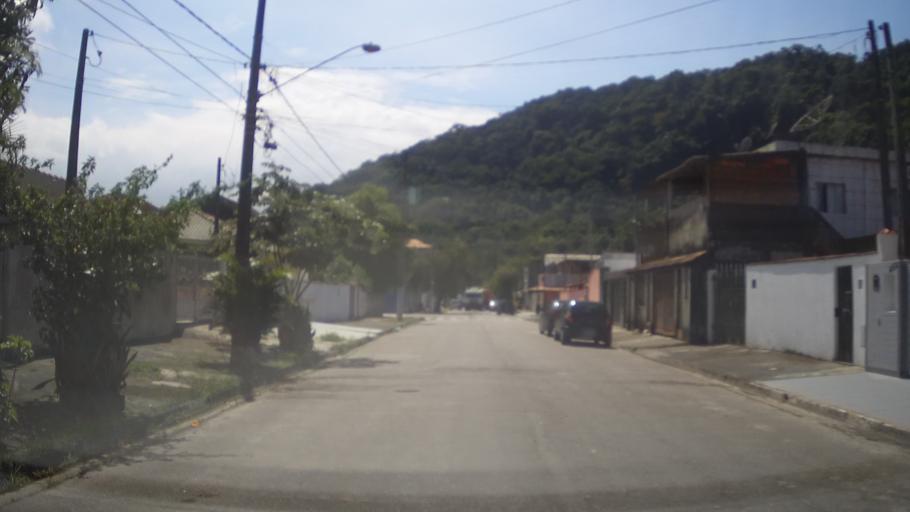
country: BR
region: Sao Paulo
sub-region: Praia Grande
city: Praia Grande
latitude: -23.9872
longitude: -46.3929
